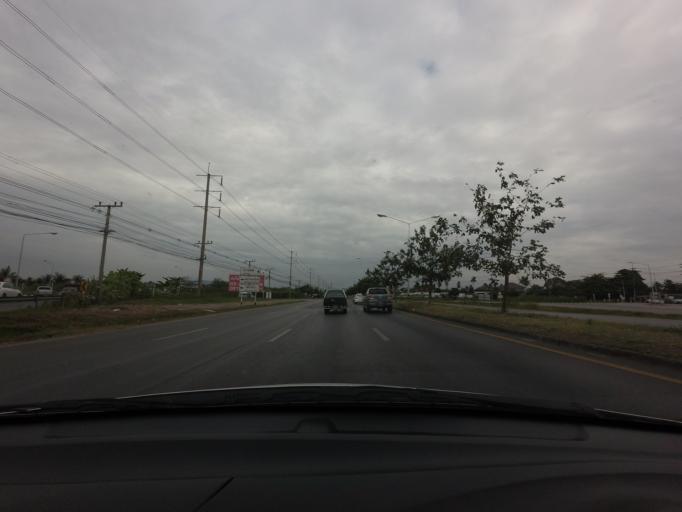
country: TH
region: Nakhon Pathom
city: Nakhon Chai Si
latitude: 13.7836
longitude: 100.2467
